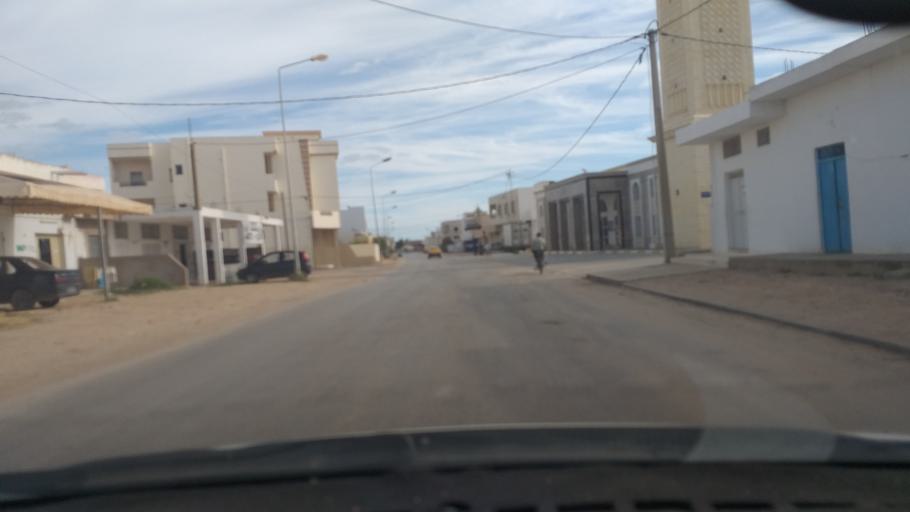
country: TN
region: Safaqis
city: Al Qarmadah
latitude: 34.7959
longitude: 10.8005
